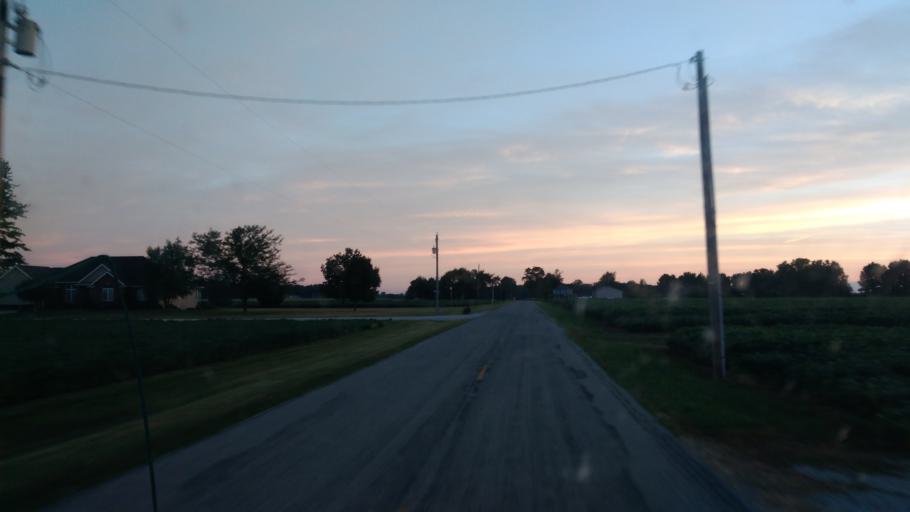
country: US
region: Indiana
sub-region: Wells County
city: Bluffton
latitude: 40.6645
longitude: -85.1263
